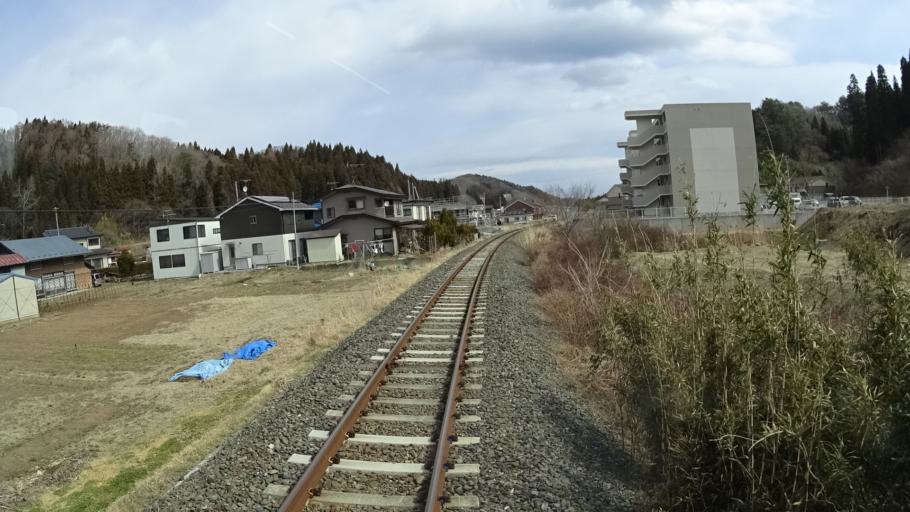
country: JP
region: Iwate
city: Miyako
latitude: 39.6149
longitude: 141.9395
